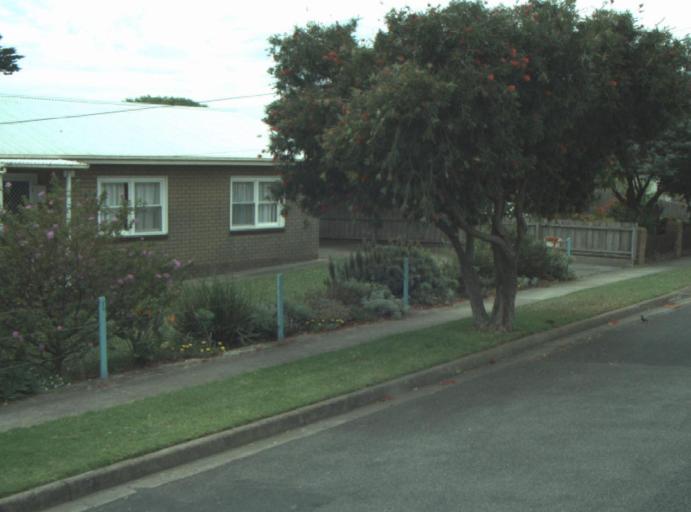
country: AU
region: Victoria
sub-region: Greater Geelong
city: Clifton Springs
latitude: -38.1184
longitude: 144.6392
